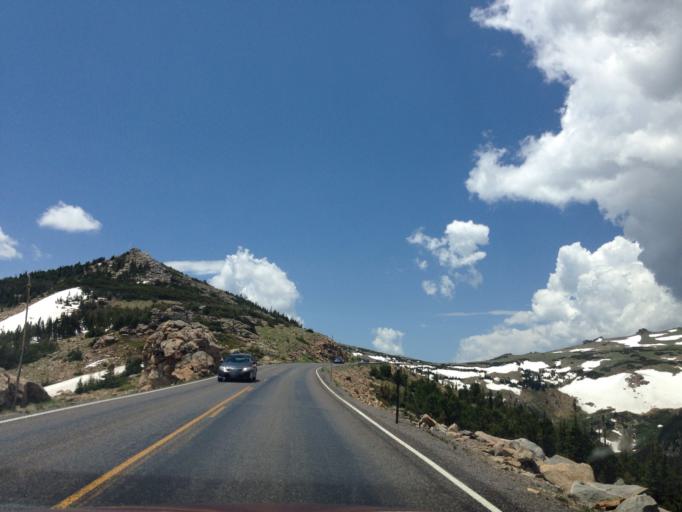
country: US
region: Colorado
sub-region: Larimer County
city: Estes Park
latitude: 40.3982
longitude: -105.6735
